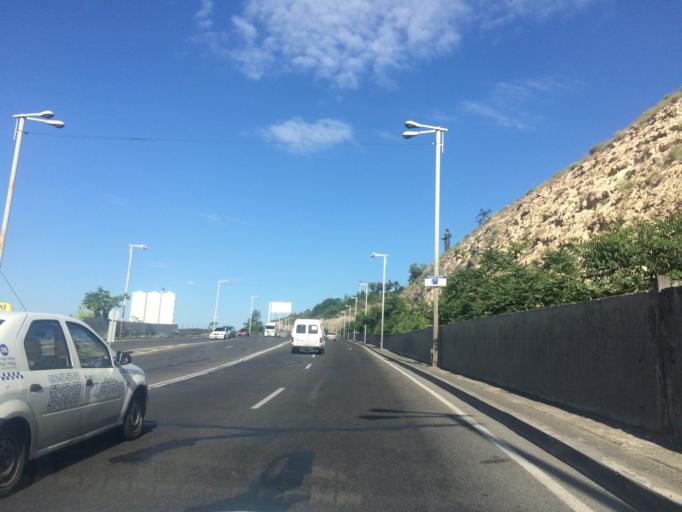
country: AM
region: Yerevan
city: Yerevan
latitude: 40.1943
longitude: 44.5300
